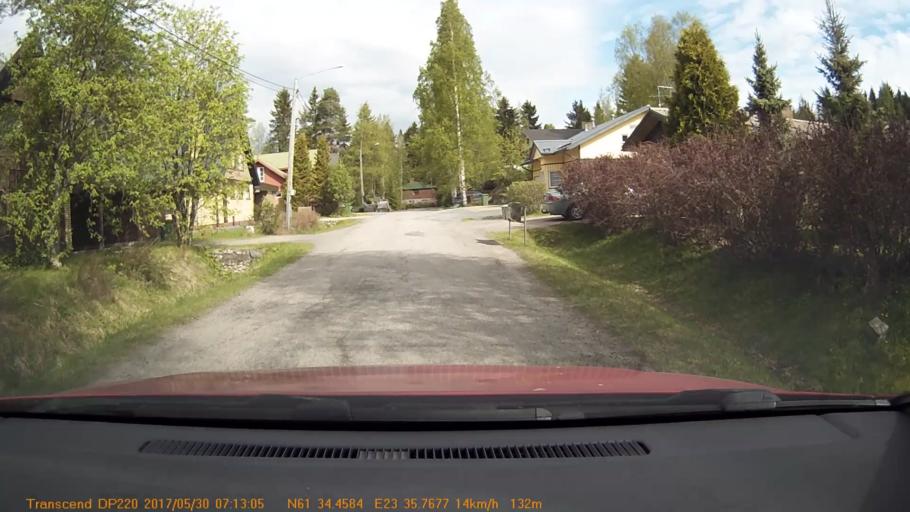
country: FI
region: Pirkanmaa
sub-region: Tampere
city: Yloejaervi
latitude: 61.5743
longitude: 23.5962
